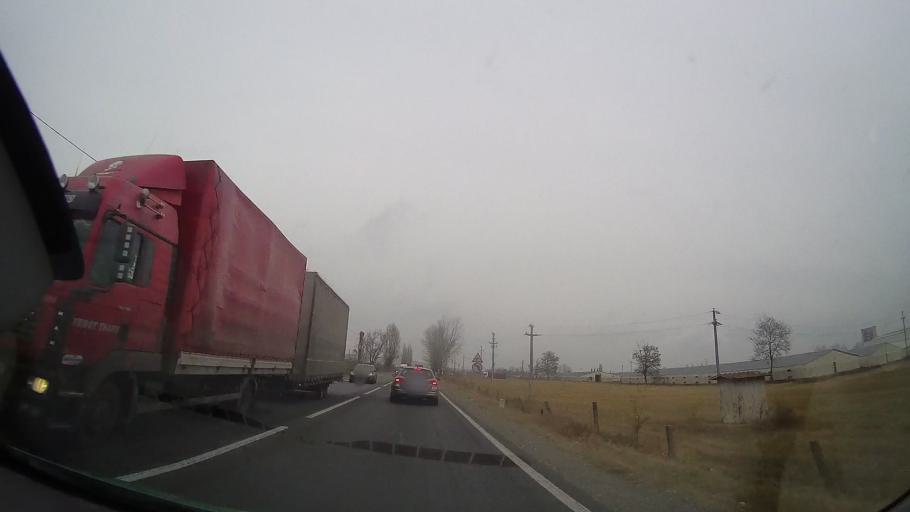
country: RO
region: Prahova
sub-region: Comuna Blejoiu
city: Ploiestiori
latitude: 44.9812
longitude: 25.9989
